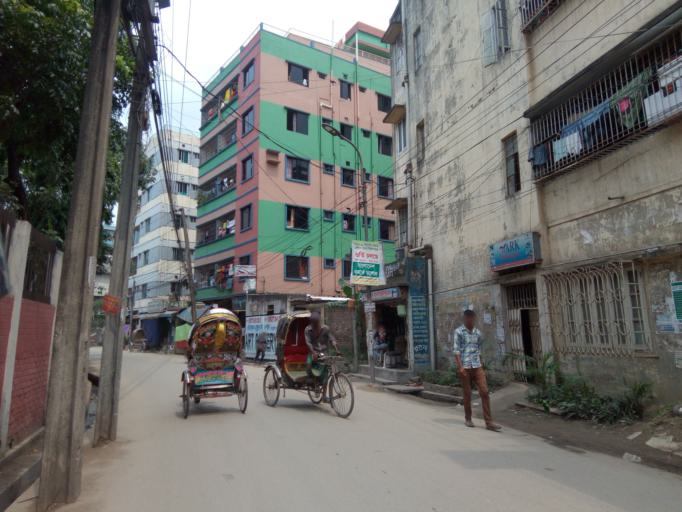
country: BD
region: Dhaka
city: Paltan
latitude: 23.7459
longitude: 90.4289
